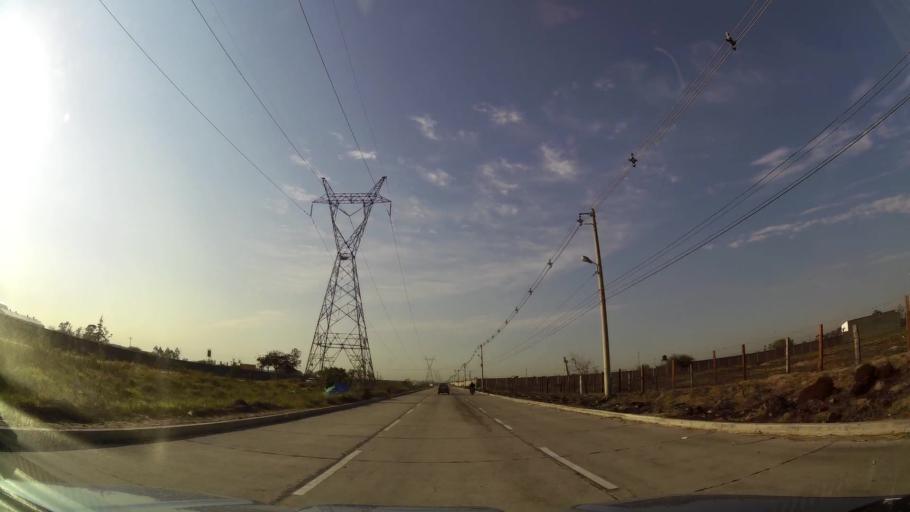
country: BO
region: Santa Cruz
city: Santa Cruz de la Sierra
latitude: -17.6778
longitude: -63.1557
